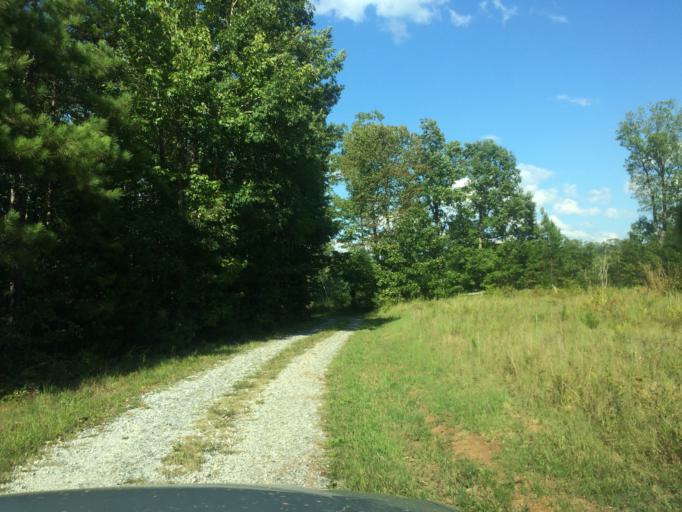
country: US
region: South Carolina
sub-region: Greenwood County
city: Ware Shoals
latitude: 34.4627
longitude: -82.1666
